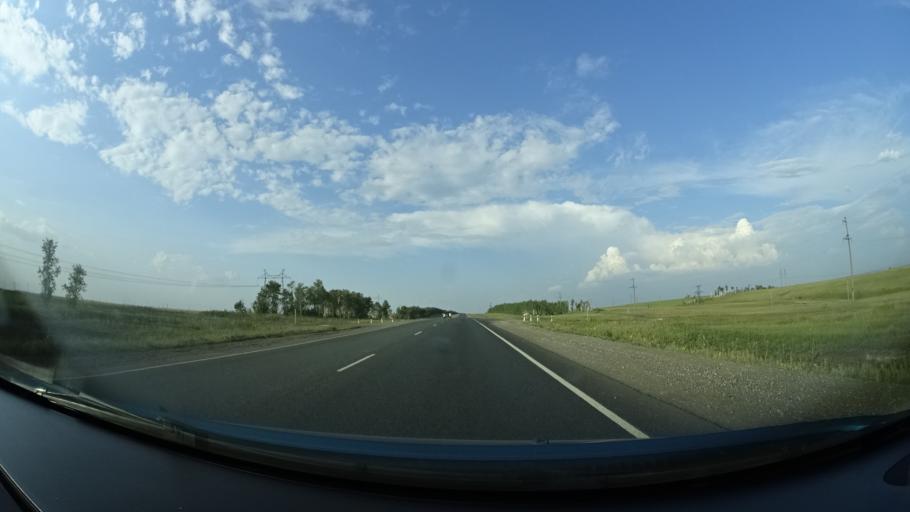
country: RU
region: Samara
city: Sukhodol
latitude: 53.7094
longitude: 50.8146
